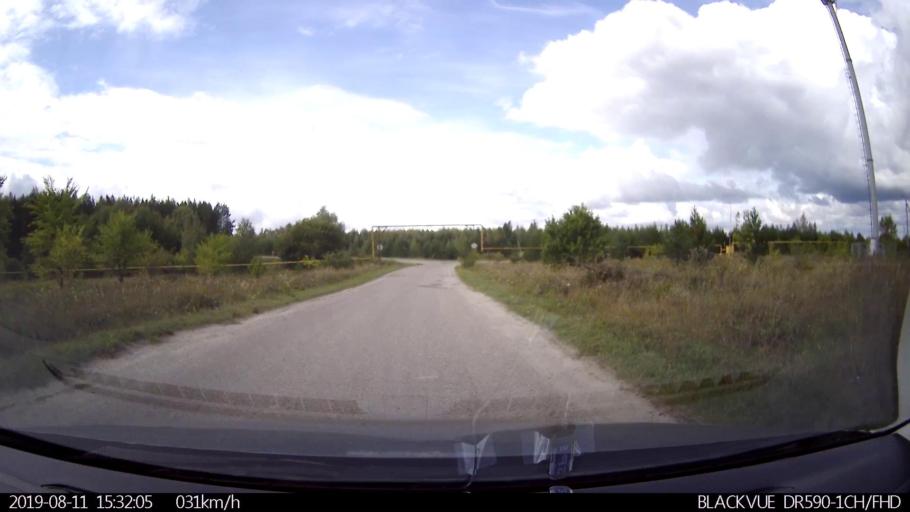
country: RU
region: Ulyanovsk
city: Ignatovka
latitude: 53.8590
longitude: 47.5758
